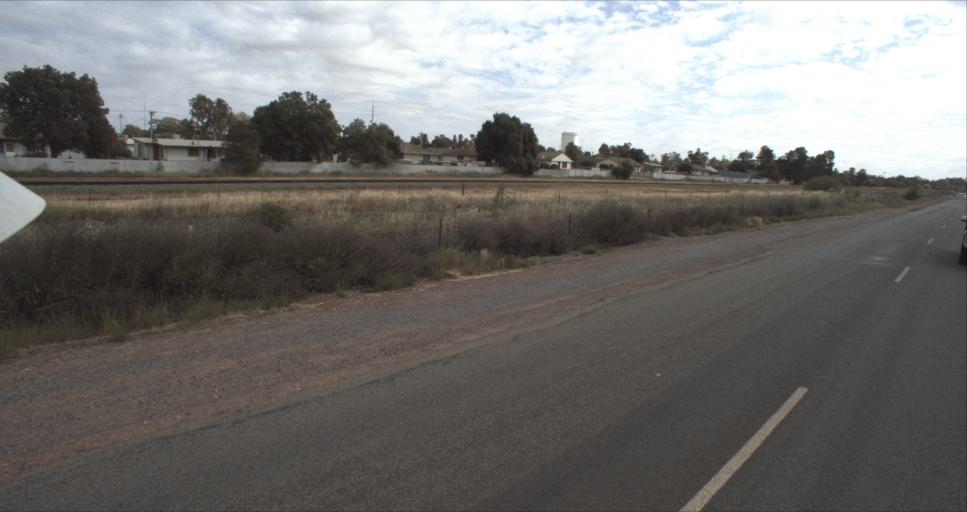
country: AU
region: New South Wales
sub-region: Leeton
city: Leeton
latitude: -34.5669
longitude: 146.3964
